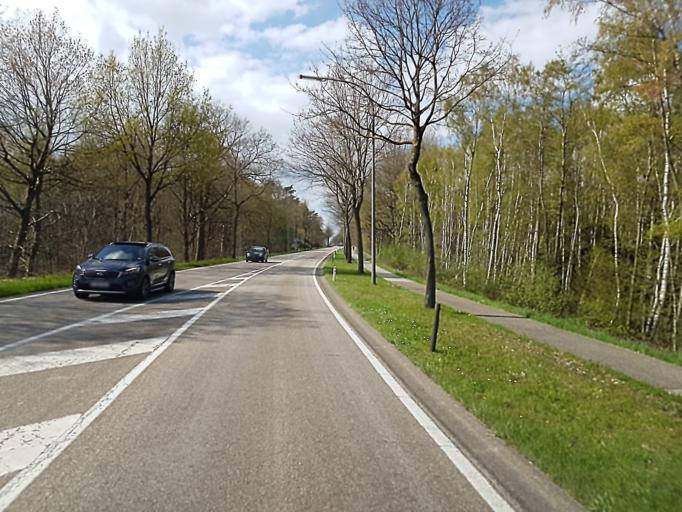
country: BE
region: Flanders
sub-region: Provincie Limburg
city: Lanaken
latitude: 50.9051
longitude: 5.6282
